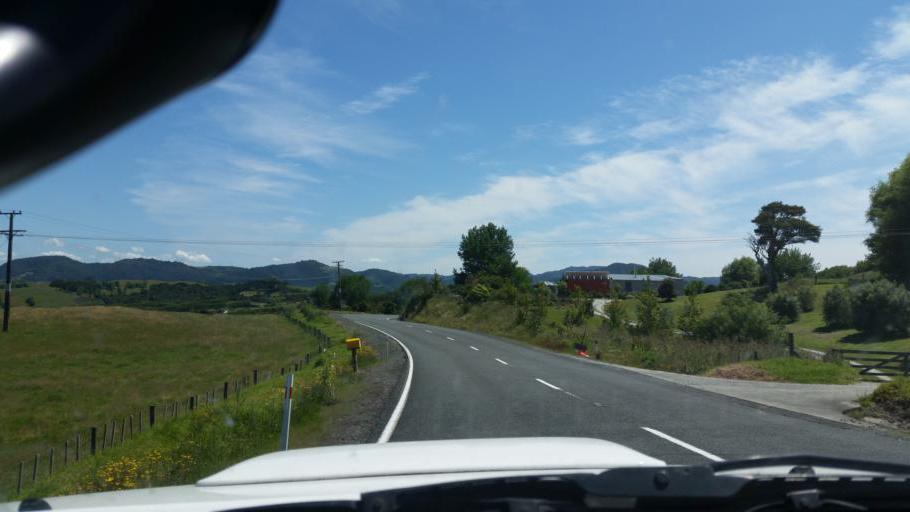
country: NZ
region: Auckland
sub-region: Auckland
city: Wellsford
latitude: -36.1810
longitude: 174.4125
